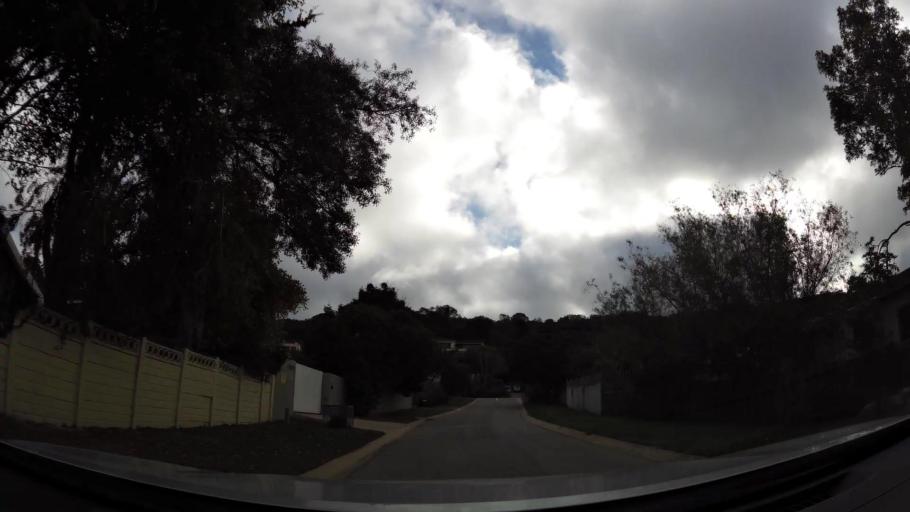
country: ZA
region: Western Cape
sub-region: Eden District Municipality
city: Plettenberg Bay
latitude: -34.0812
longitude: 23.3630
